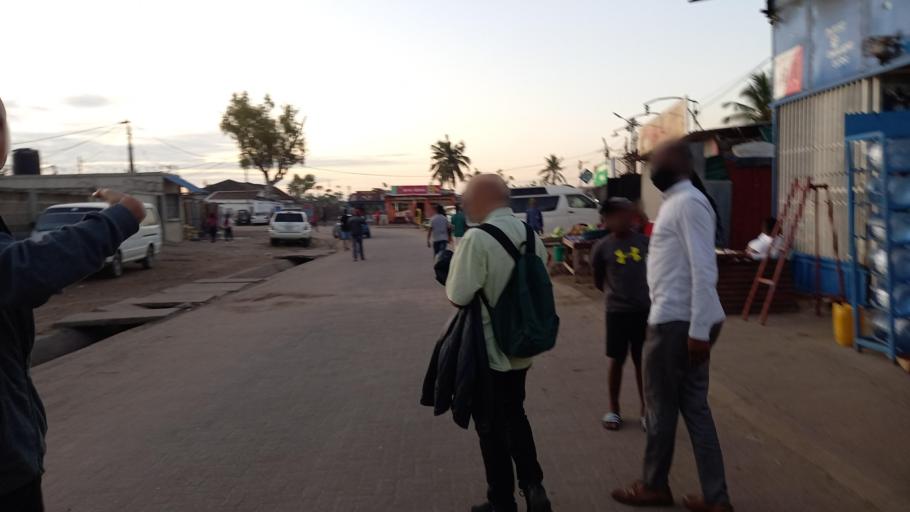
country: MZ
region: Maputo City
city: Maputo
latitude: -25.9512
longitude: 32.5714
